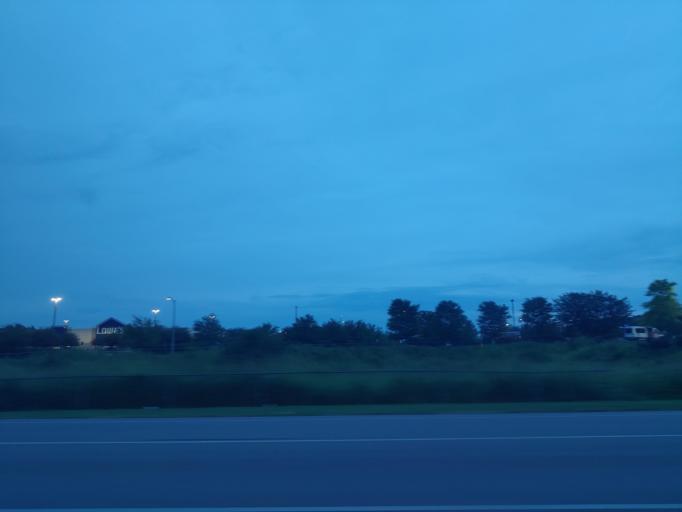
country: US
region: Kentucky
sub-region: Scott County
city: Georgetown
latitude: 38.2279
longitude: -84.5353
